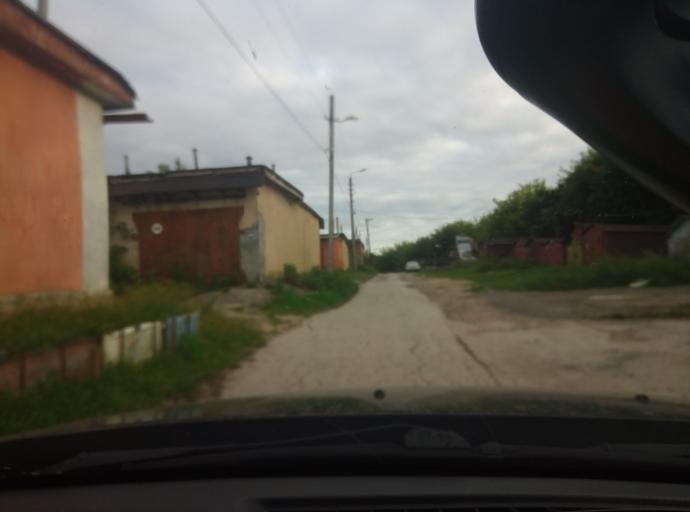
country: RU
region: Tula
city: Mendeleyevskiy
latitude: 54.1665
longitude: 37.5601
